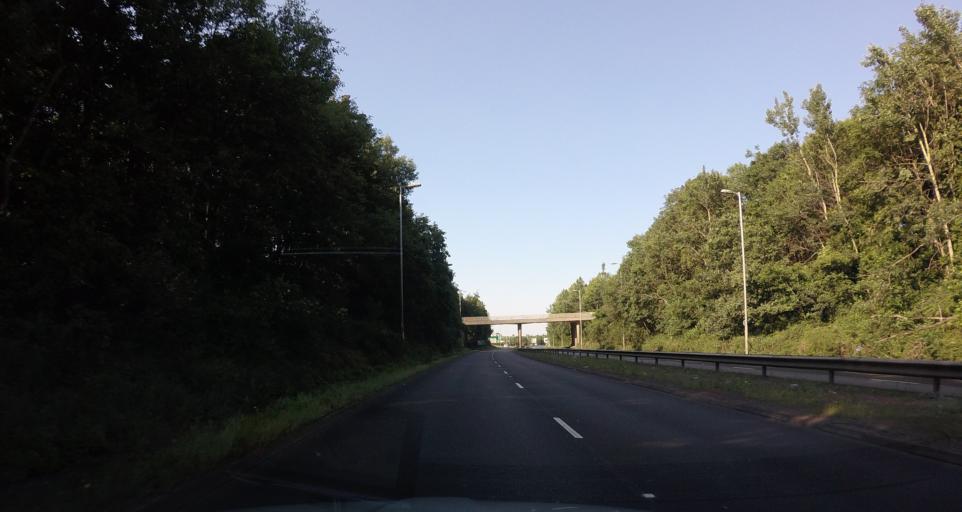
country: GB
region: Scotland
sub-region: North Lanarkshire
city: Bellshill
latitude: 55.8207
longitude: -4.0397
